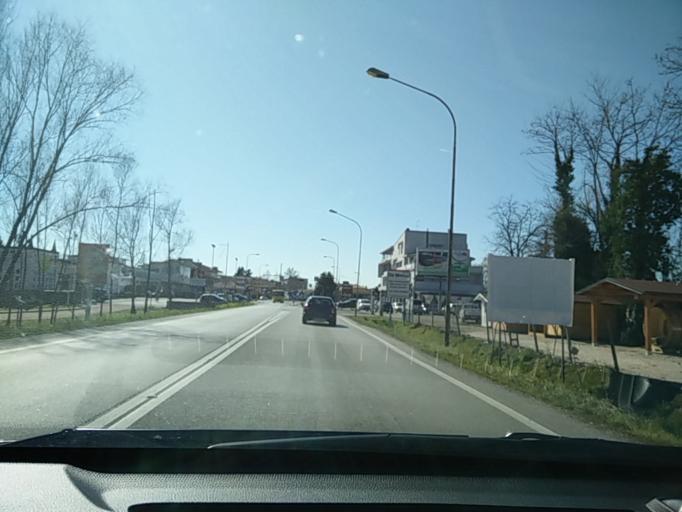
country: IT
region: Friuli Venezia Giulia
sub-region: Provincia di Pordenone
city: Sacile
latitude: 45.9573
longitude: 12.4970
